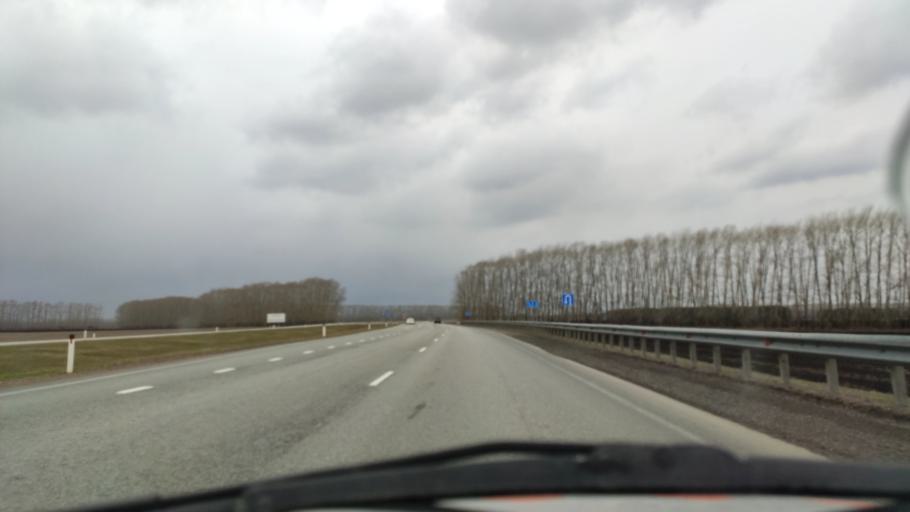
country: RU
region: Bashkortostan
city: Asanovo
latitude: 54.9822
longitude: 55.5421
